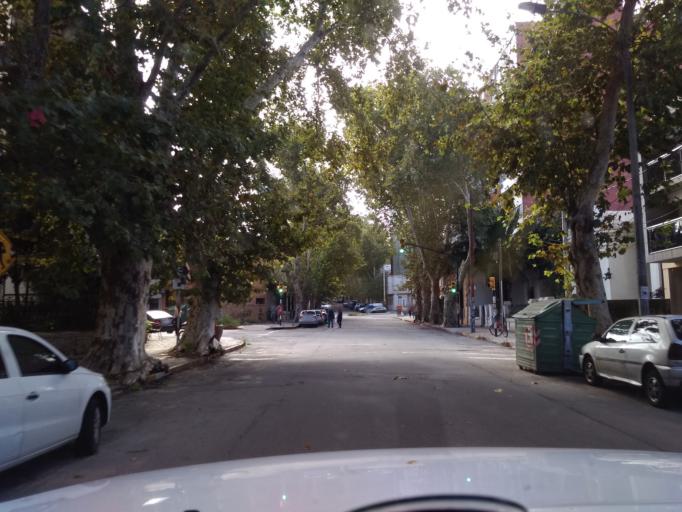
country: UY
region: Montevideo
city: Montevideo
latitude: -34.9060
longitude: -56.1513
